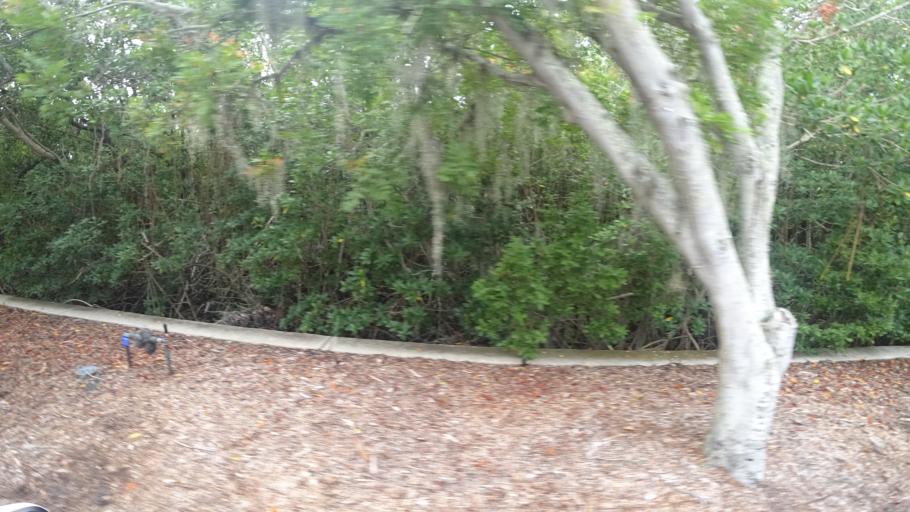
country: US
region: Florida
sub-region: Manatee County
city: Longboat Key
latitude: 27.4264
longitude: -82.6708
